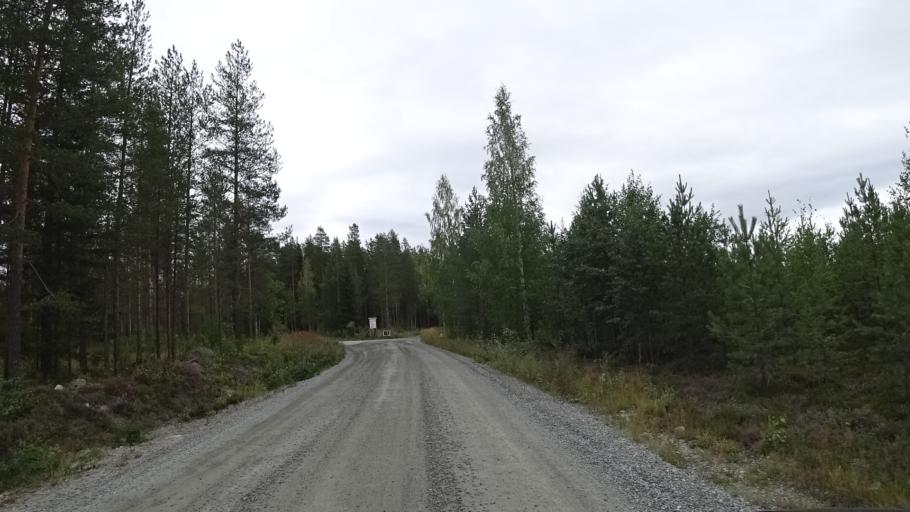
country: FI
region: North Karelia
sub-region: Pielisen Karjala
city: Lieksa
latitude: 63.3628
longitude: 30.3897
